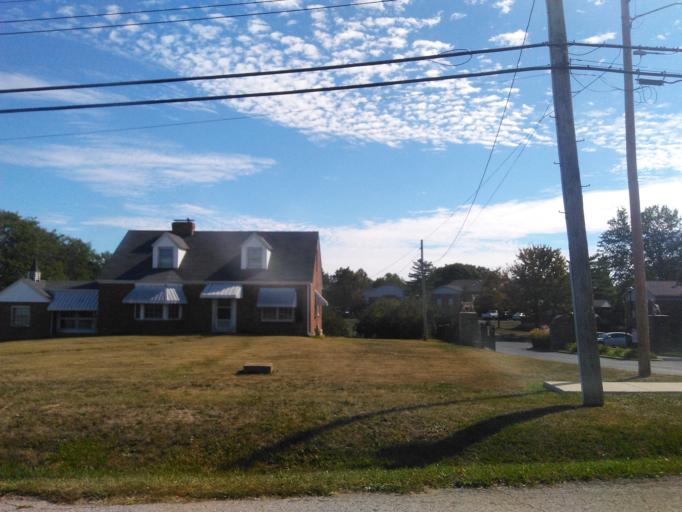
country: US
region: Missouri
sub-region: Saint Louis County
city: Concord
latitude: 38.4996
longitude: -90.3808
